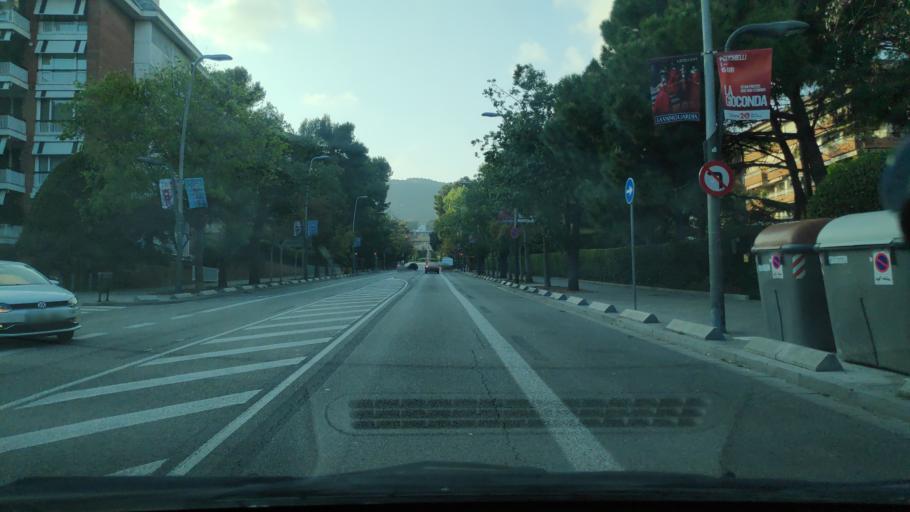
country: ES
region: Catalonia
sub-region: Provincia de Barcelona
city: les Corts
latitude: 41.3924
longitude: 2.1160
